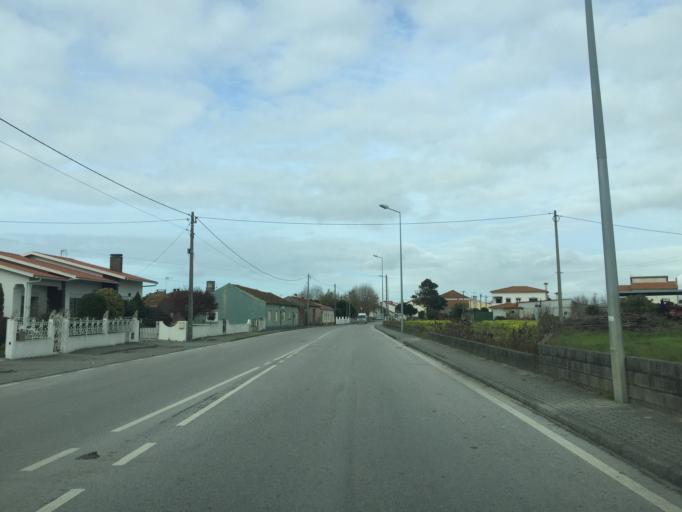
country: PT
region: Coimbra
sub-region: Figueira da Foz
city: Lavos
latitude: 40.0250
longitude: -8.8201
